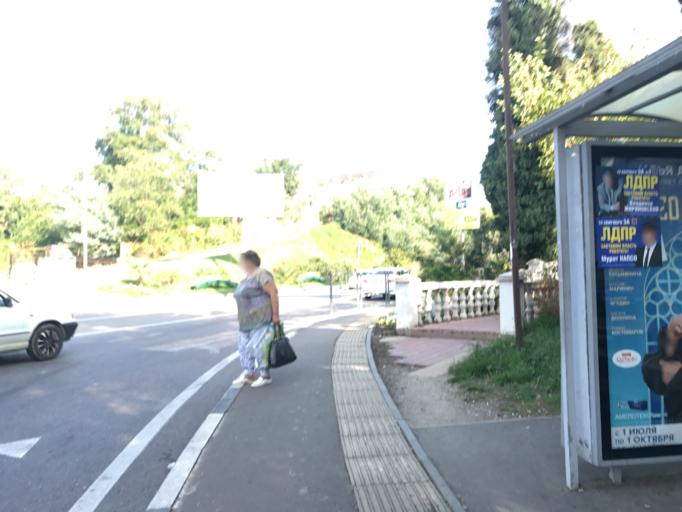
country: RU
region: Krasnodarskiy
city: Adler
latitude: 43.4213
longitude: 39.9391
